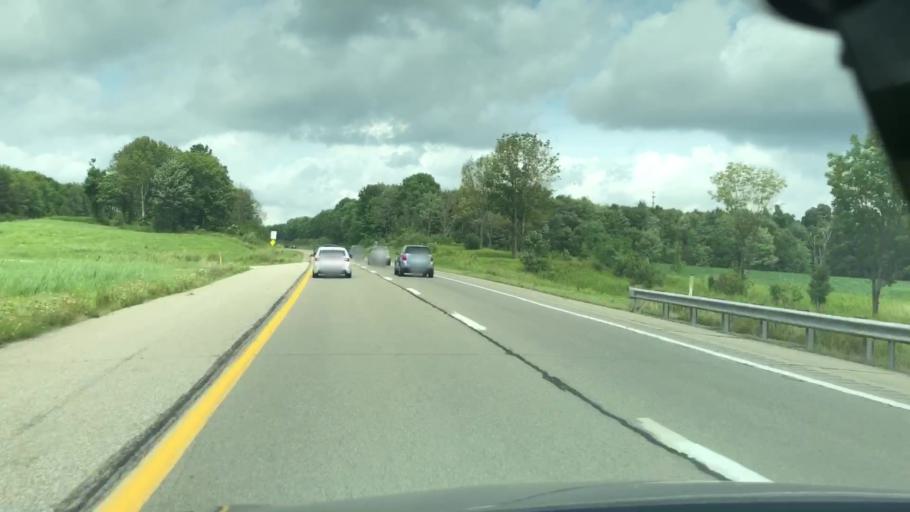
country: US
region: Pennsylvania
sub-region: Erie County
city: Edinboro
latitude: 41.7829
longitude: -80.1802
